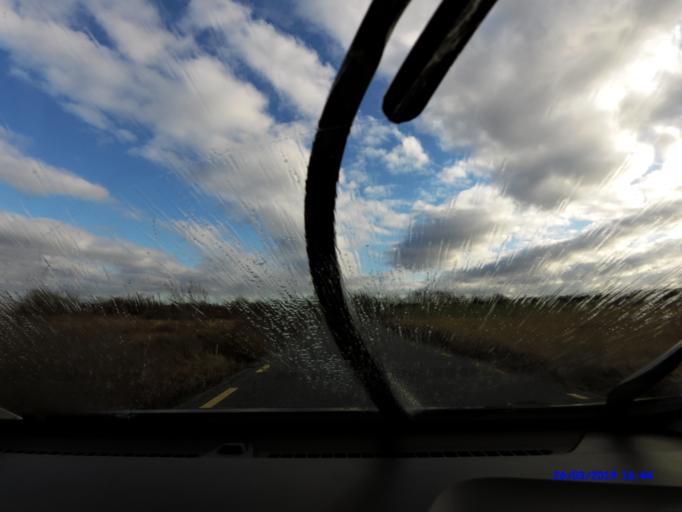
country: IE
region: Connaught
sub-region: Maigh Eo
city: Ballyhaunis
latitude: 53.8480
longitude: -8.7660
